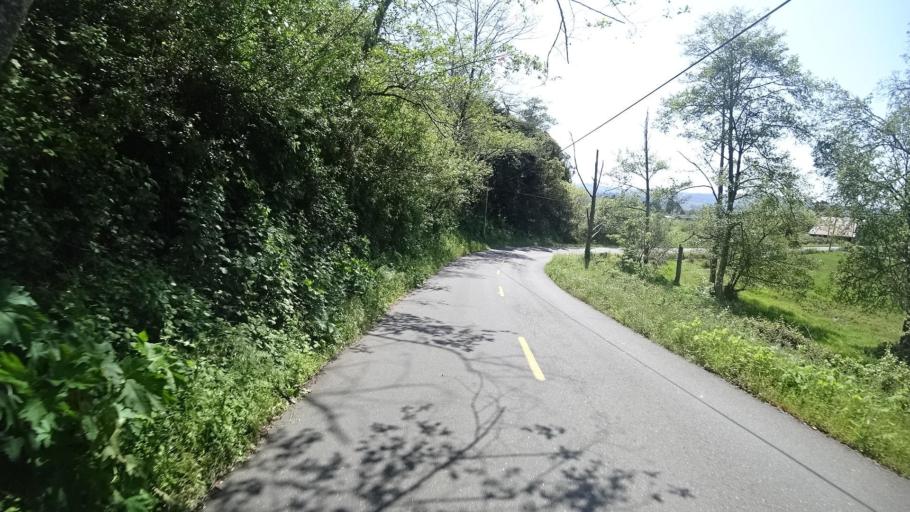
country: US
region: California
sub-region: Humboldt County
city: Fortuna
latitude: 40.5633
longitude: -124.1422
